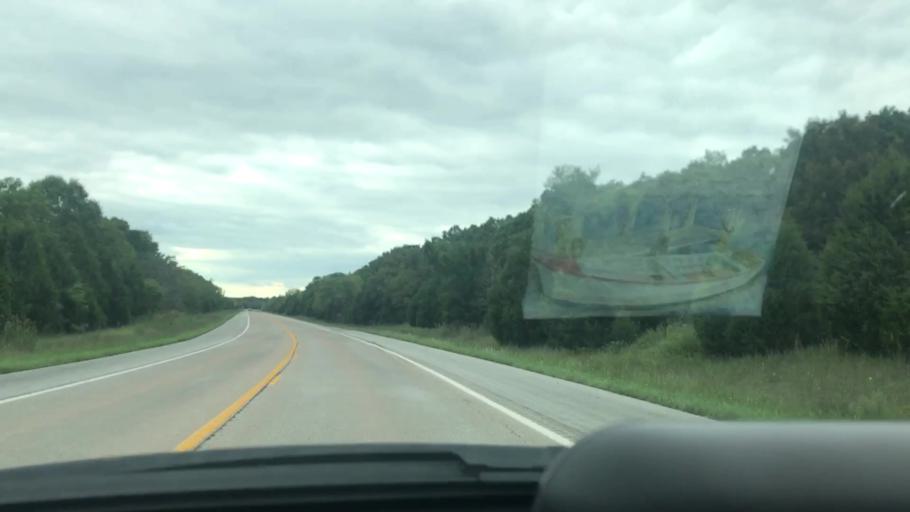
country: US
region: Missouri
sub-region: Benton County
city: Warsaw
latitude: 38.2086
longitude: -93.3315
